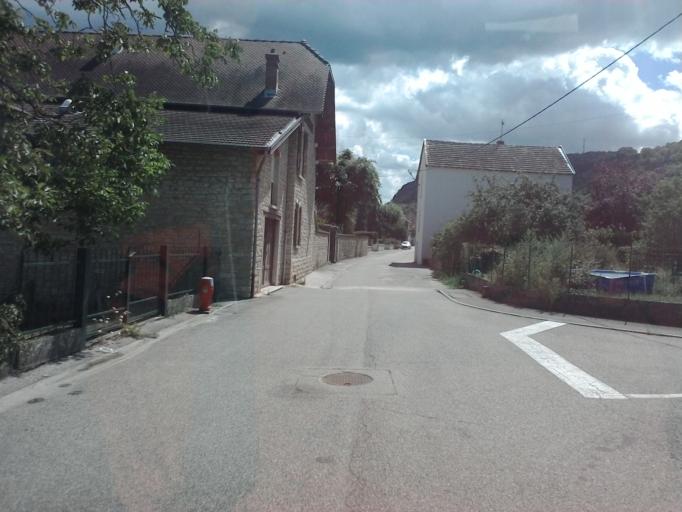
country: FR
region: Rhone-Alpes
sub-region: Departement de l'Ain
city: Saint-Sorlin-en-Bugey
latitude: 45.8755
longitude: 5.3643
